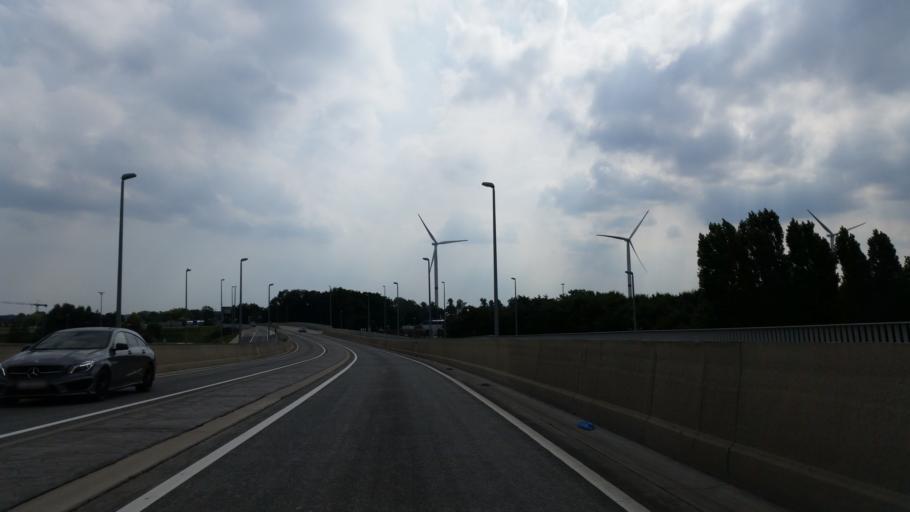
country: BE
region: Flanders
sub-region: Provincie Antwerpen
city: Westerlo
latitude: 51.1327
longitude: 4.9387
